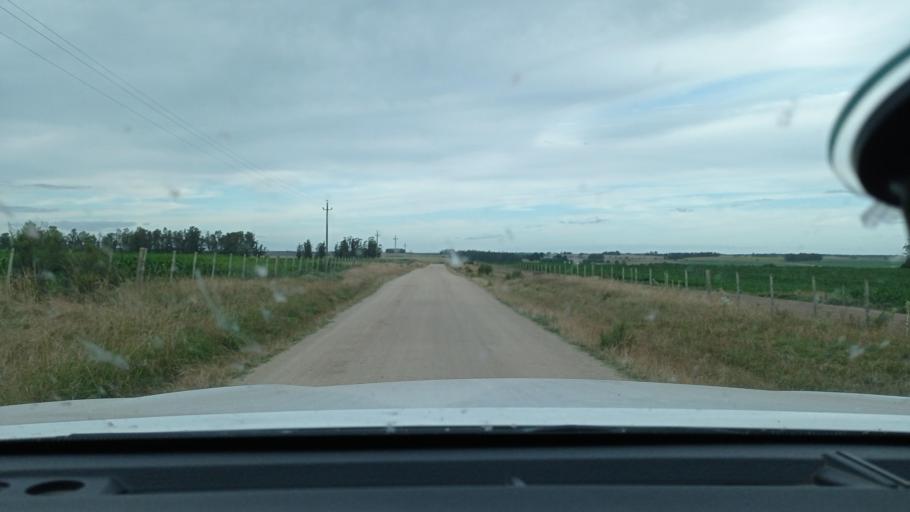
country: UY
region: Florida
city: Casupa
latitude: -34.1032
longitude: -55.7534
